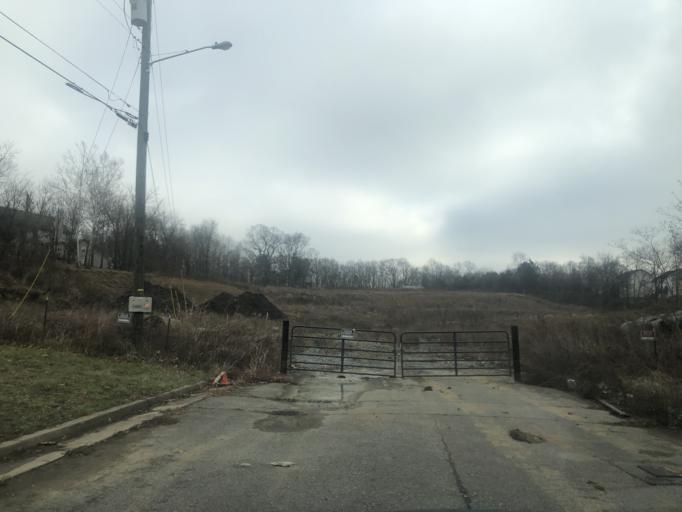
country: US
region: Tennessee
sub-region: Rutherford County
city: La Vergne
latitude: 36.0699
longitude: -86.6489
